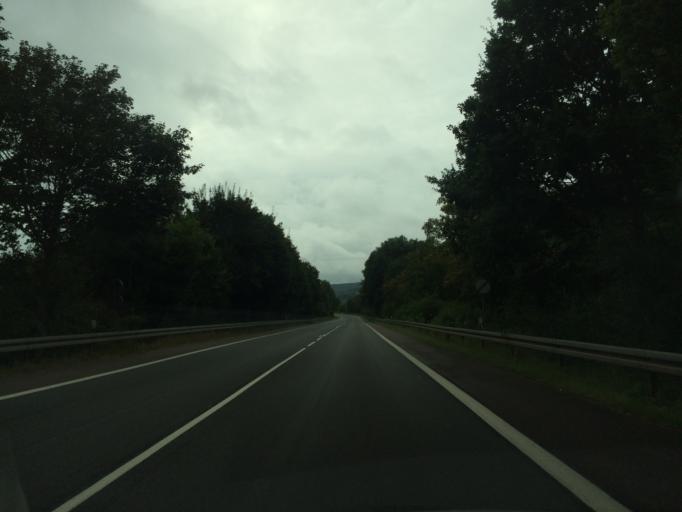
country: DE
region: Saarland
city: Merzig
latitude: 49.4281
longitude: 6.6328
